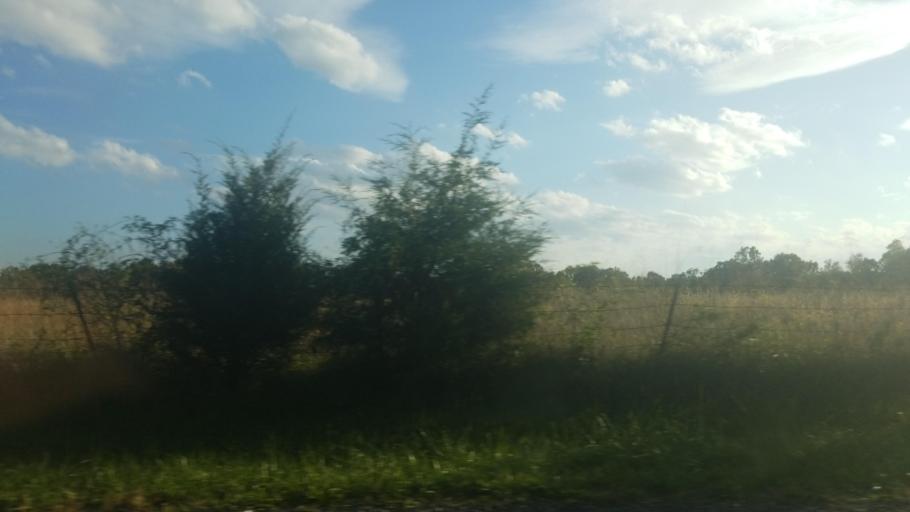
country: US
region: Illinois
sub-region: Saline County
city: Carrier Mills
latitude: 37.7717
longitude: -88.7490
